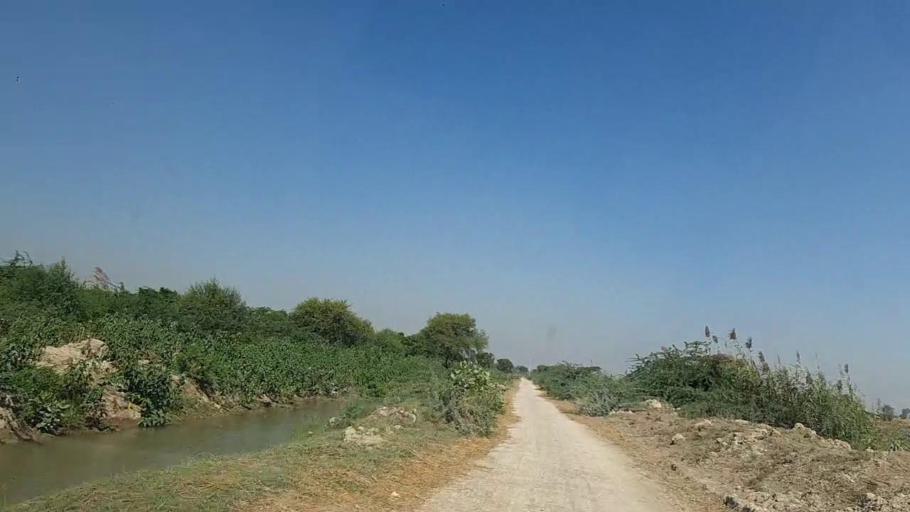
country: PK
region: Sindh
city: Daro Mehar
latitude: 24.7664
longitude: 68.1552
